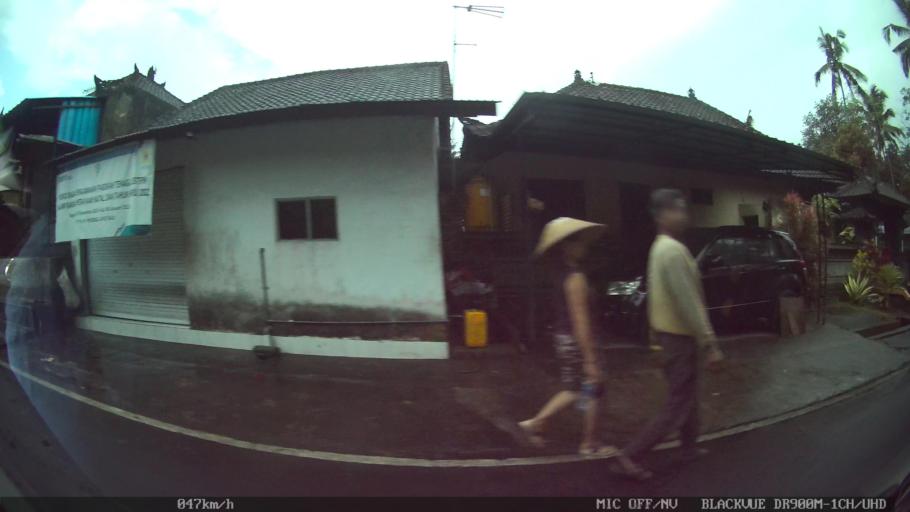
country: ID
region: Bali
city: Pegongan
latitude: -8.4902
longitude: 115.2380
